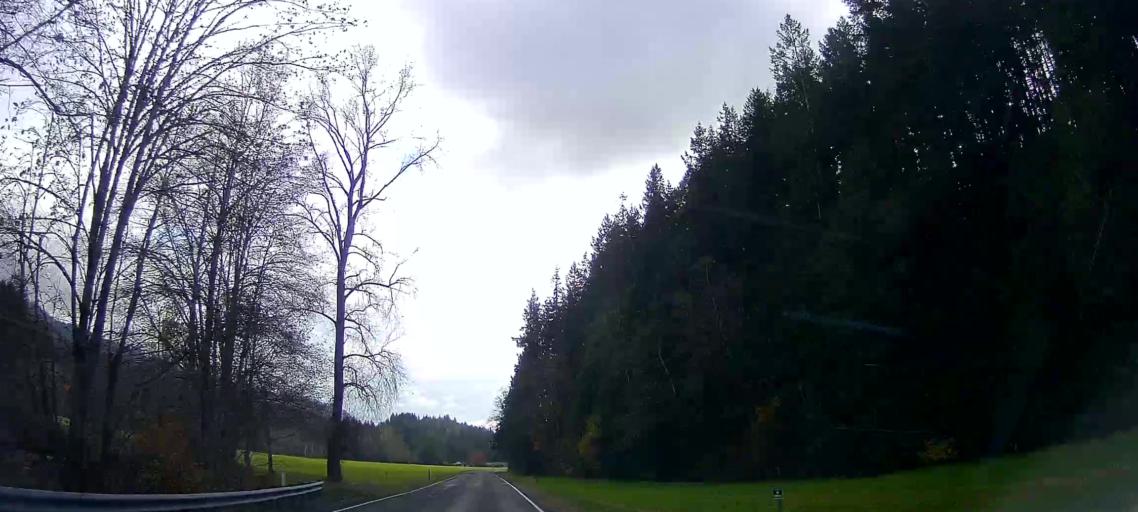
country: US
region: Washington
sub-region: Skagit County
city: Big Lake
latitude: 48.4184
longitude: -122.2085
